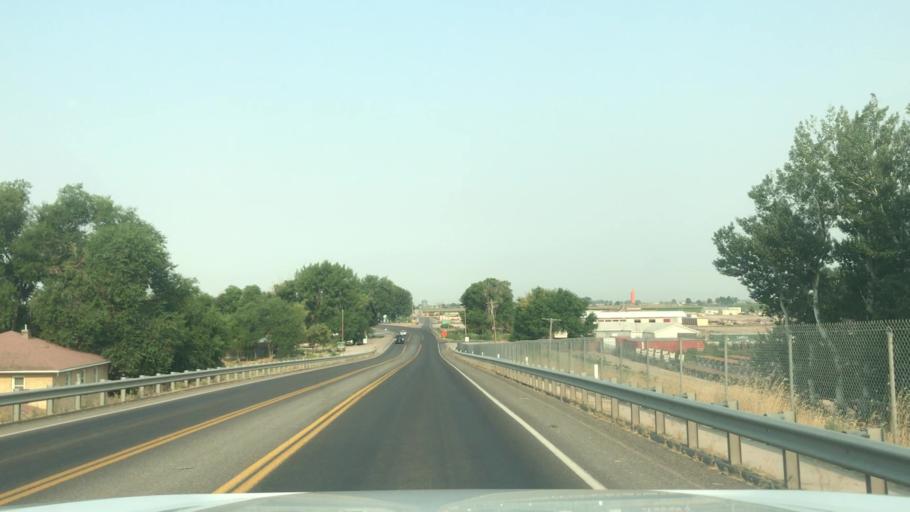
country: US
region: Utah
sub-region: Millard County
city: Delta
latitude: 39.3525
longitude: -112.5874
